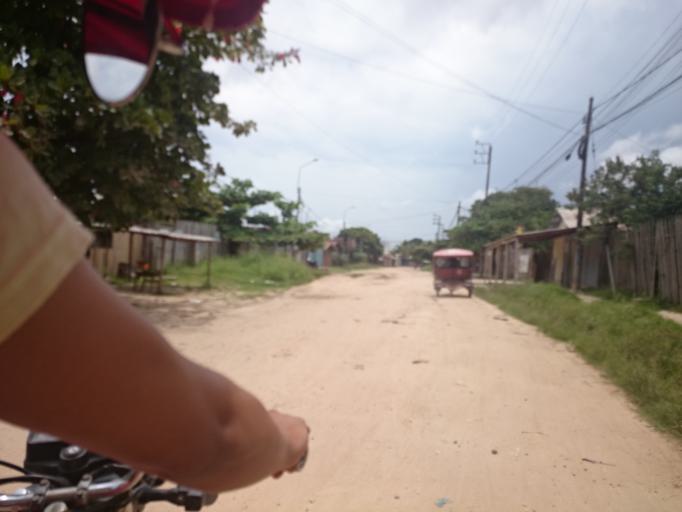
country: PE
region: Ucayali
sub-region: Provincia de Coronel Portillo
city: Pucallpa
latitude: -8.3769
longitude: -74.5606
